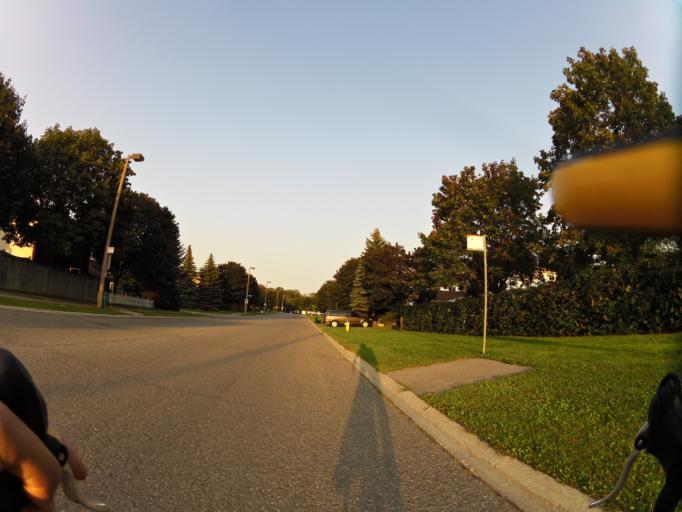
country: CA
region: Ontario
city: Bells Corners
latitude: 45.3481
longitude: -75.9357
